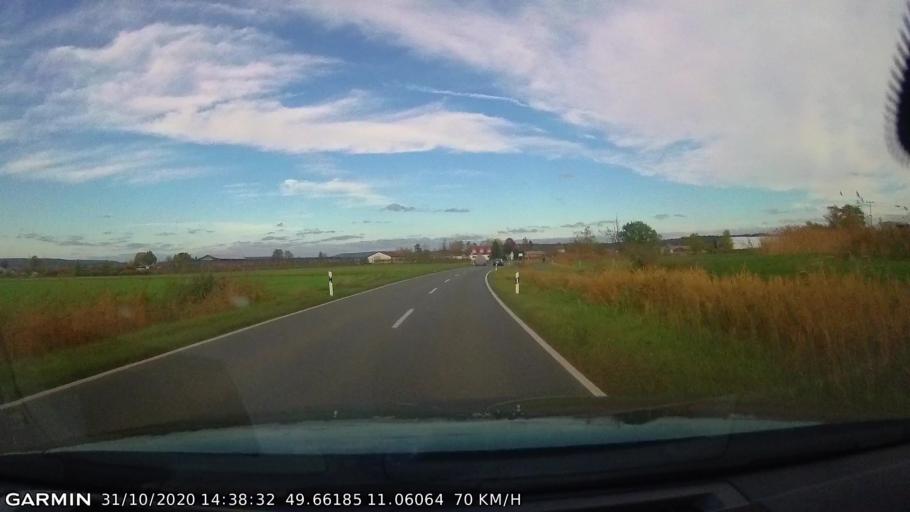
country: DE
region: Bavaria
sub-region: Upper Franconia
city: Poxdorf
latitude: 49.6620
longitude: 11.0603
